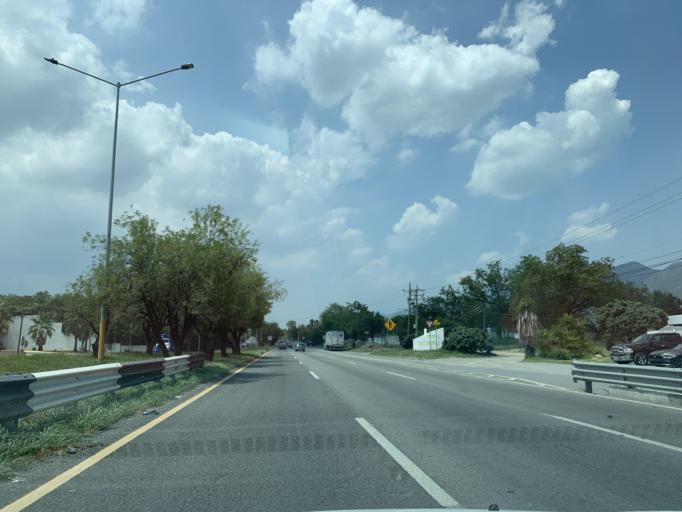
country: MX
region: Nuevo Leon
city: Santiago
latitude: 25.4411
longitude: -100.1546
